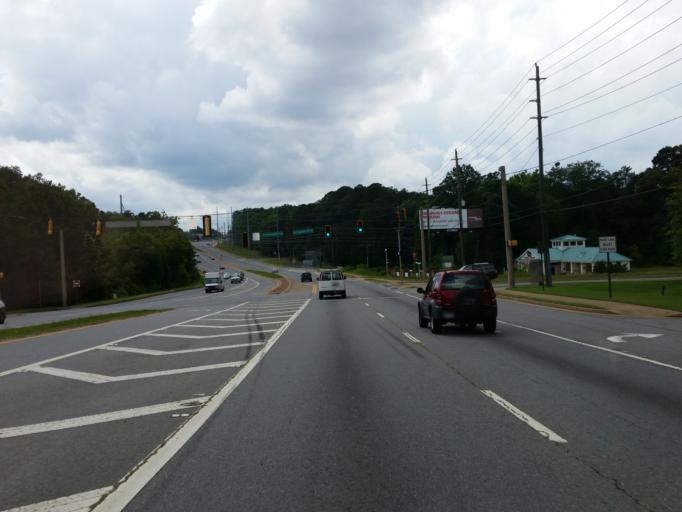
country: US
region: Georgia
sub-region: Cherokee County
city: Woodstock
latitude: 34.0867
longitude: -84.5095
